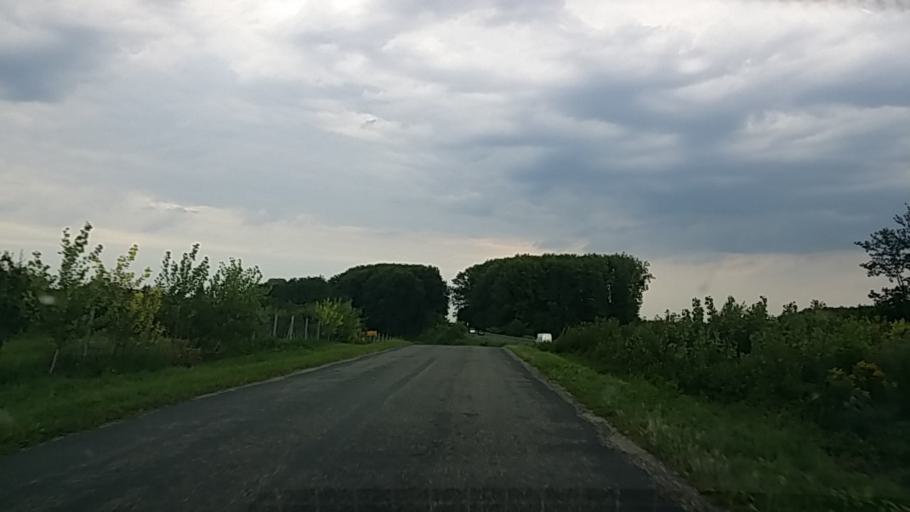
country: HU
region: Zala
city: Zalakomar
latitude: 46.5052
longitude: 17.0961
